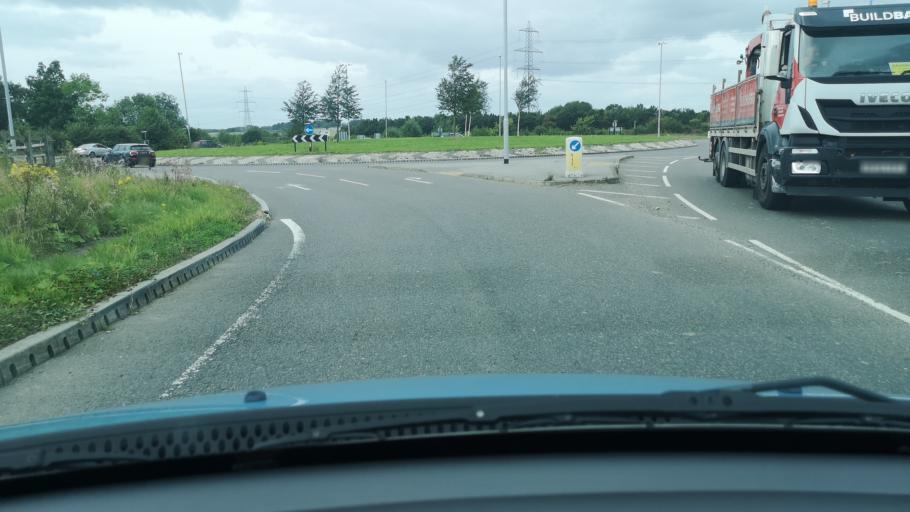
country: GB
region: England
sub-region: City and Borough of Wakefield
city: North Elmsall
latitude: 53.6077
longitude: -1.2865
